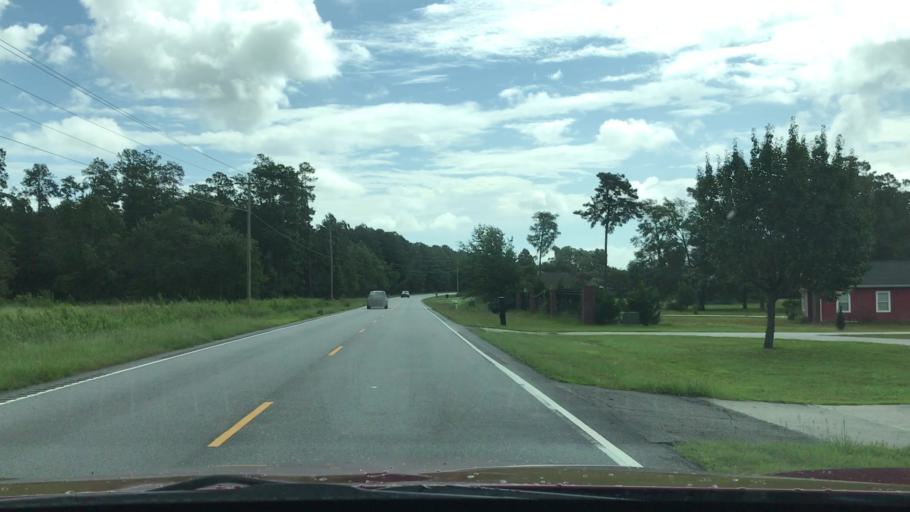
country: US
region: South Carolina
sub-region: Horry County
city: North Myrtle Beach
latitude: 33.9249
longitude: -78.7858
